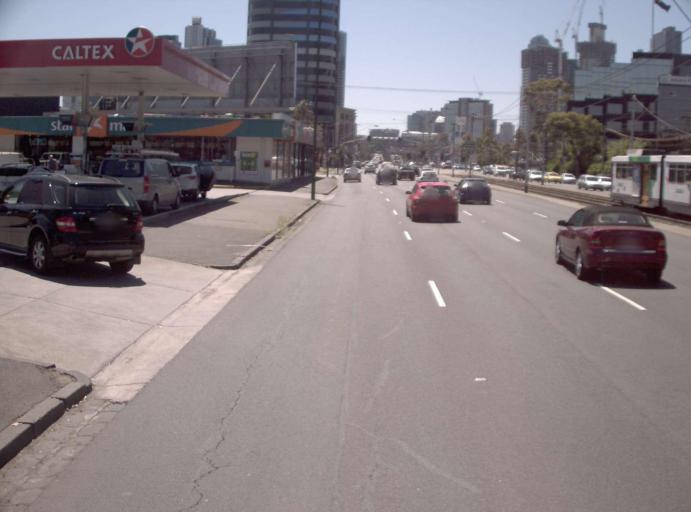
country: AU
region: Victoria
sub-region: Port Phillip
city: South Melbourne
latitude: -37.8324
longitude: 144.9666
